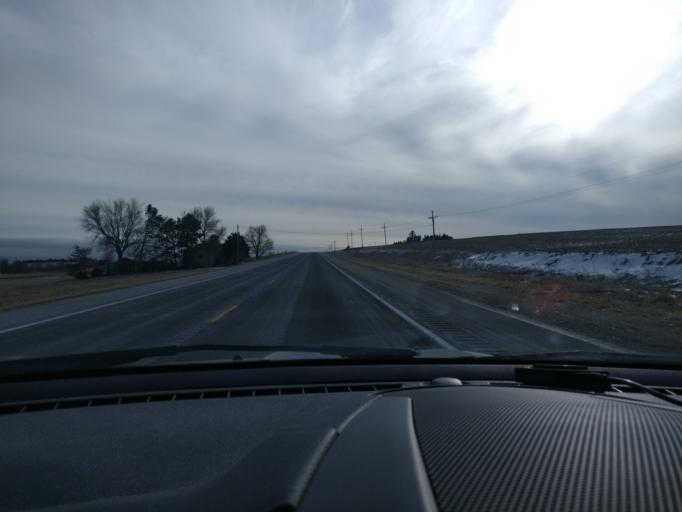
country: US
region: Nebraska
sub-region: Saunders County
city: Yutan
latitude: 41.2956
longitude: -96.5030
